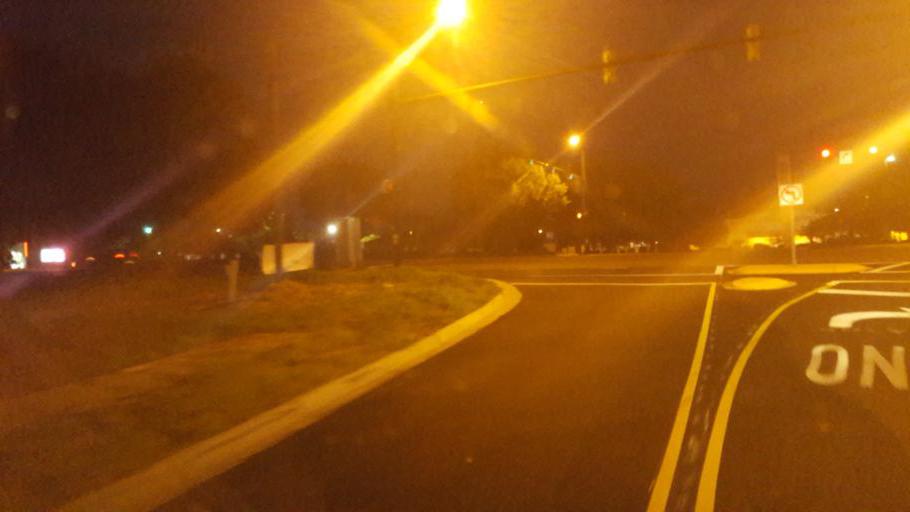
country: US
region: South Carolina
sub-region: York County
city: Fort Mill
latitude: 34.9767
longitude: -80.9823
